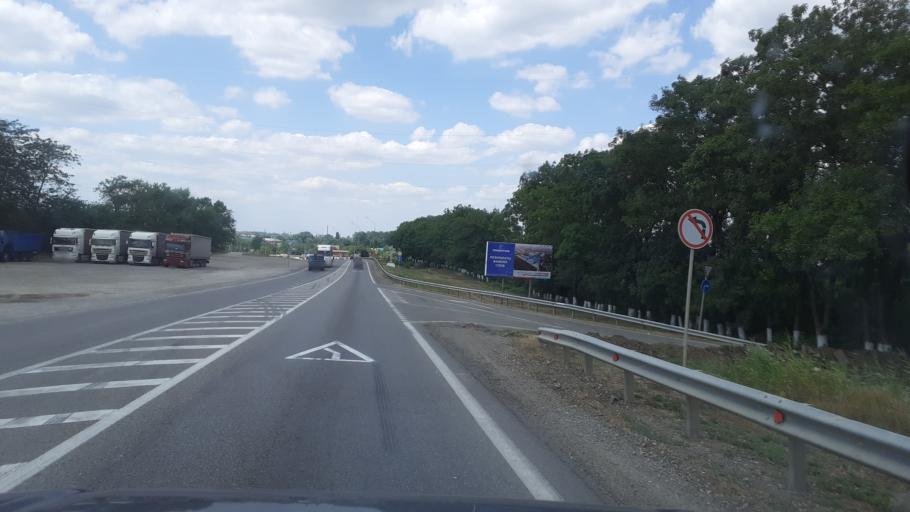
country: RU
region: Krasnodarskiy
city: Il'skiy
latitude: 44.8523
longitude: 38.5965
